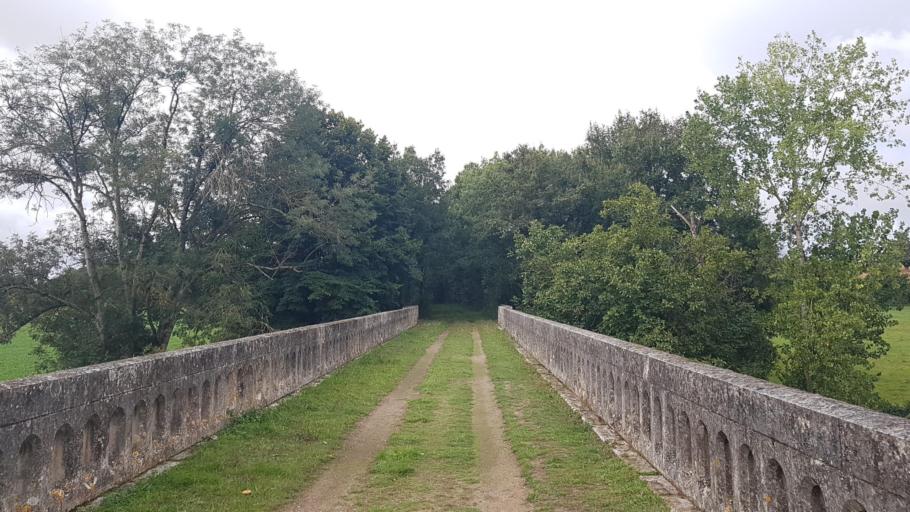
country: FR
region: Poitou-Charentes
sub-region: Departement de la Vienne
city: Saint-Savin
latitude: 46.5803
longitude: 0.8767
